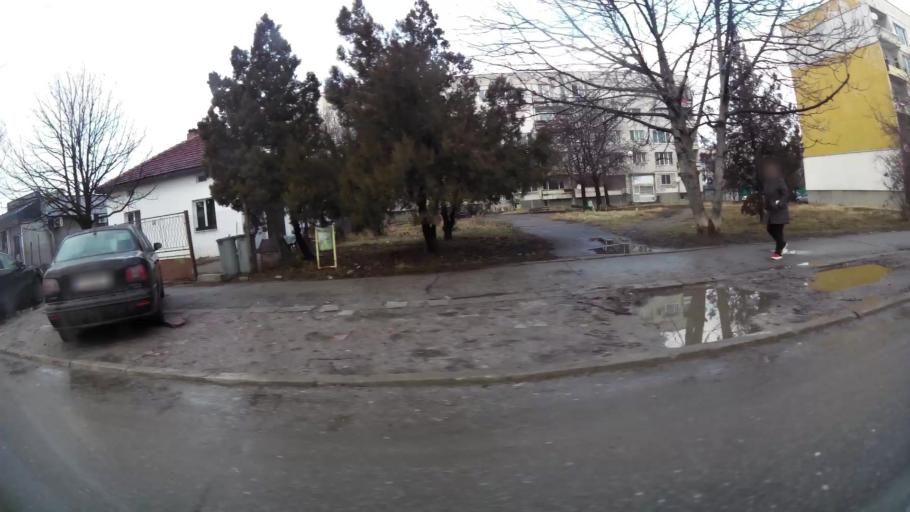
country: BG
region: Sofia-Capital
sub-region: Stolichna Obshtina
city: Sofia
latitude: 42.7399
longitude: 23.3442
